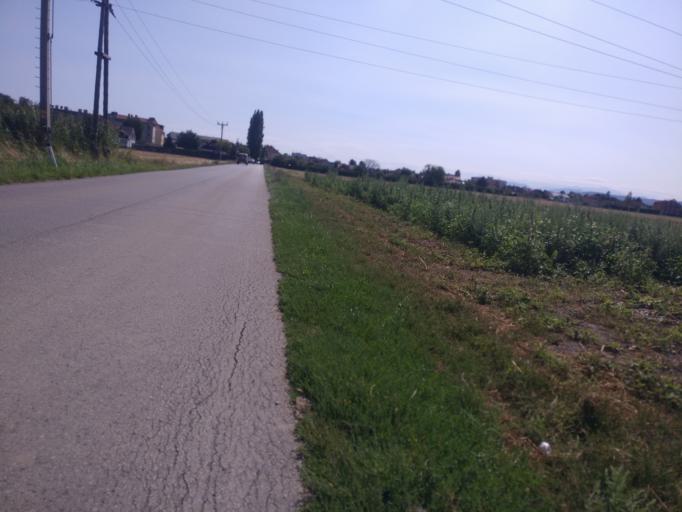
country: AT
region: Lower Austria
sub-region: Politischer Bezirk Modling
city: Guntramsdorf
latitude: 48.0324
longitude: 16.3075
